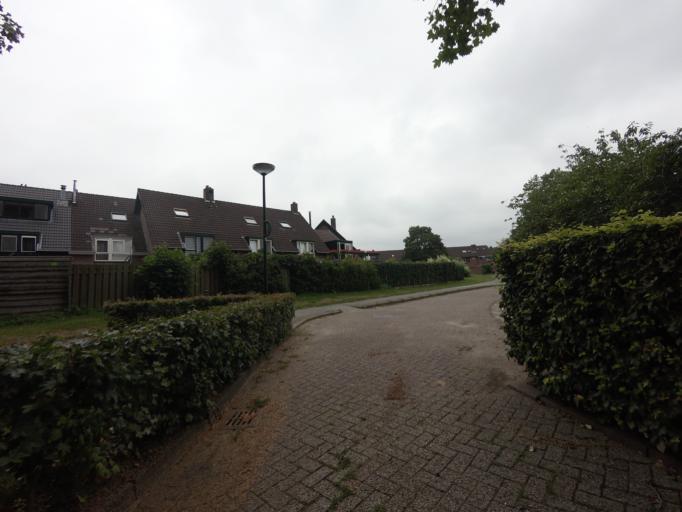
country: NL
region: Utrecht
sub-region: Gemeente Wijk bij Duurstede
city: Wijk bij Duurstede
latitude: 51.9828
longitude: 5.3472
